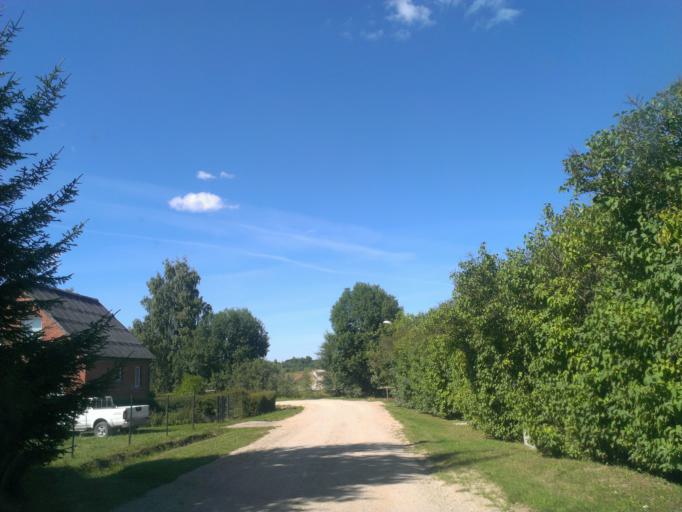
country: LV
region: Malpils
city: Malpils
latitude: 57.0116
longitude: 24.9679
